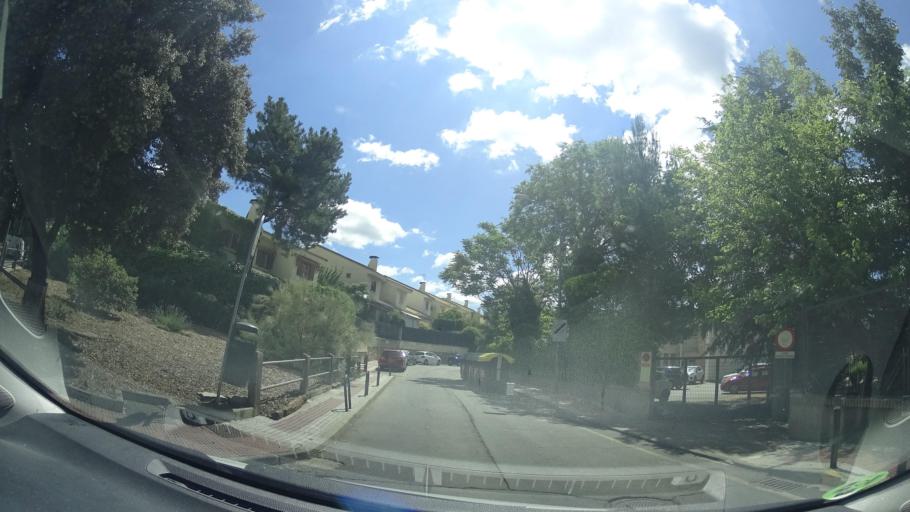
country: ES
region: Madrid
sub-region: Provincia de Madrid
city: Collado-Villalba
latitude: 40.6270
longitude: -4.0009
